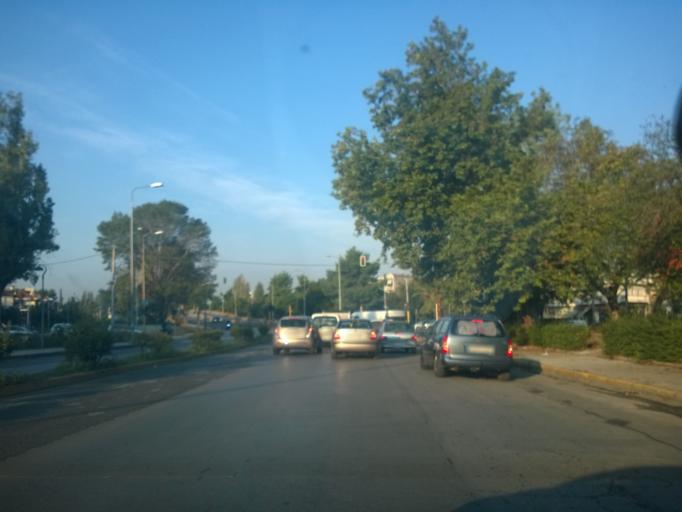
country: GR
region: Central Macedonia
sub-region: Nomos Thessalonikis
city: Evosmos
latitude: 40.6601
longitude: 22.9092
